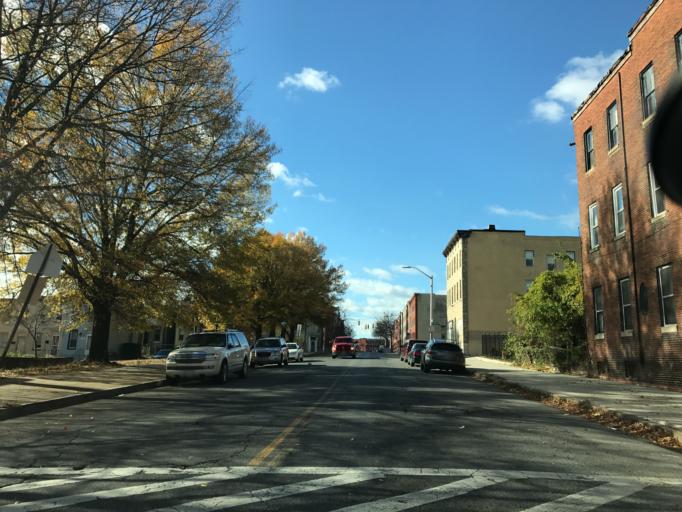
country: US
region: Maryland
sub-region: City of Baltimore
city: Baltimore
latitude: 39.2988
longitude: -76.6305
